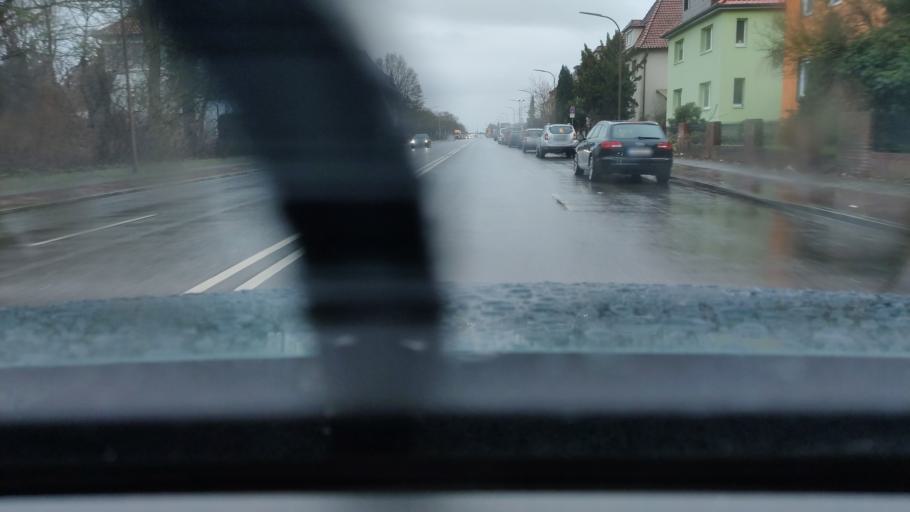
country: DE
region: Lower Saxony
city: Peine
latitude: 52.3132
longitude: 10.2324
